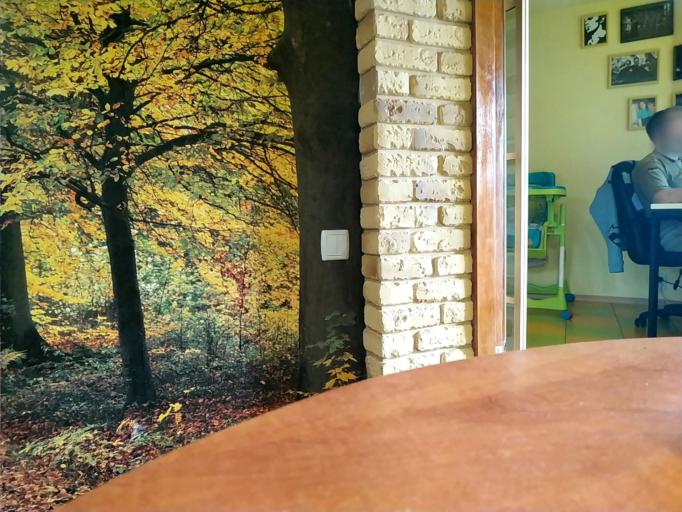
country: RU
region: Tverskaya
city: Vasil'yevskiy Mokh
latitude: 57.2044
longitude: 35.7399
